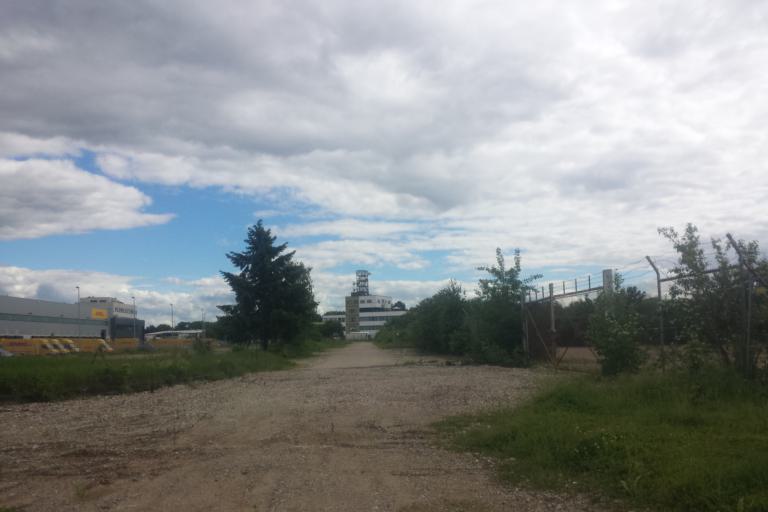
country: DE
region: Hesse
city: Viernheim
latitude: 49.5137
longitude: 8.5520
